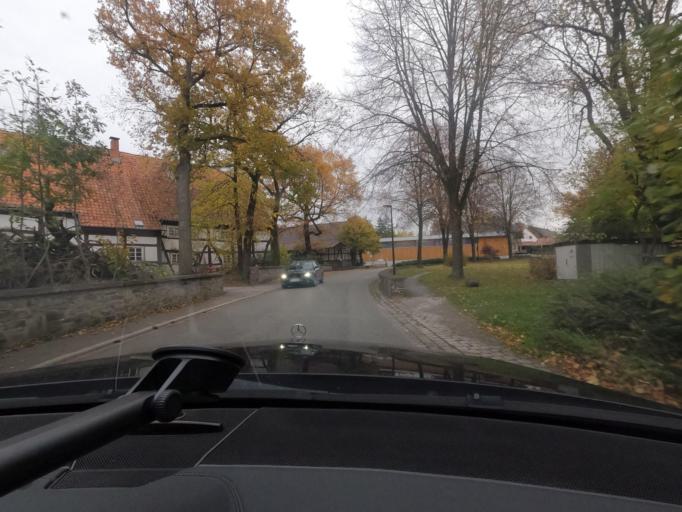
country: DE
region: North Rhine-Westphalia
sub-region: Regierungsbezirk Arnsberg
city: Mohnesee
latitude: 51.4818
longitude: 8.1998
